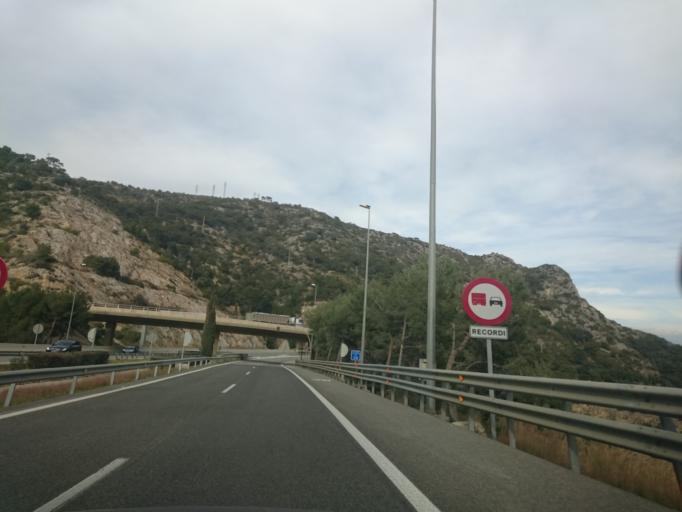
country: ES
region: Catalonia
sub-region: Provincia de Barcelona
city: Castelldefels
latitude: 41.2517
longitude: 1.8926
